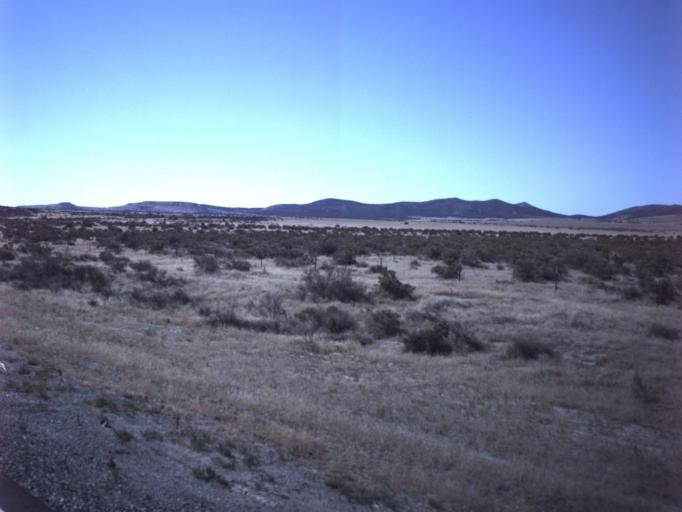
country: US
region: Utah
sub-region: Tooele County
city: Grantsville
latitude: 40.2967
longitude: -112.7426
